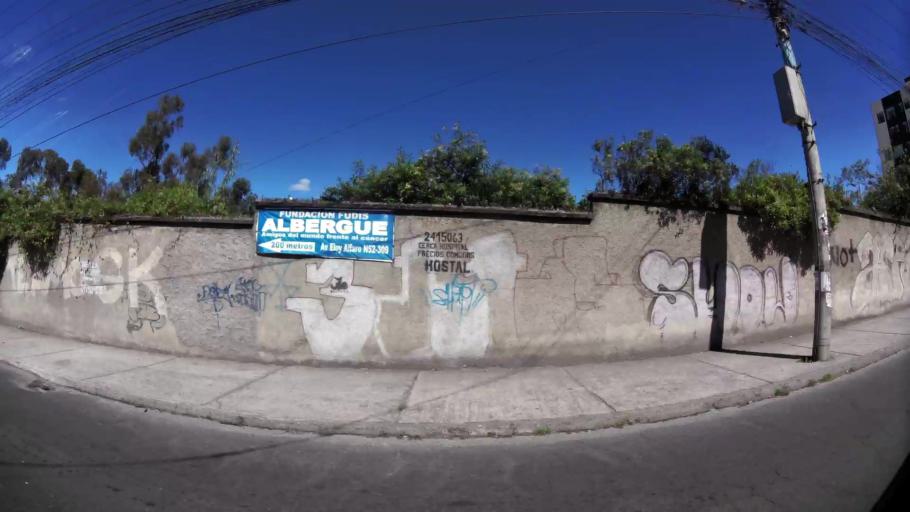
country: EC
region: Pichincha
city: Quito
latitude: -0.1365
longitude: -78.4702
